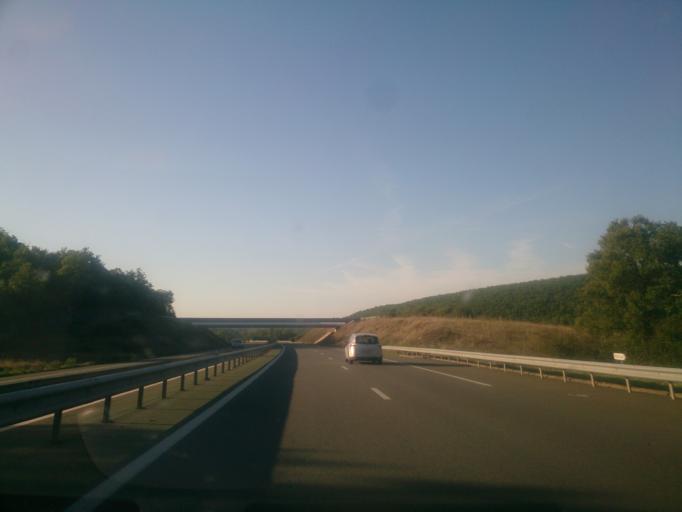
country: FR
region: Midi-Pyrenees
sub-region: Departement du Lot
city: Le Vigan
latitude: 44.7719
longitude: 1.5383
